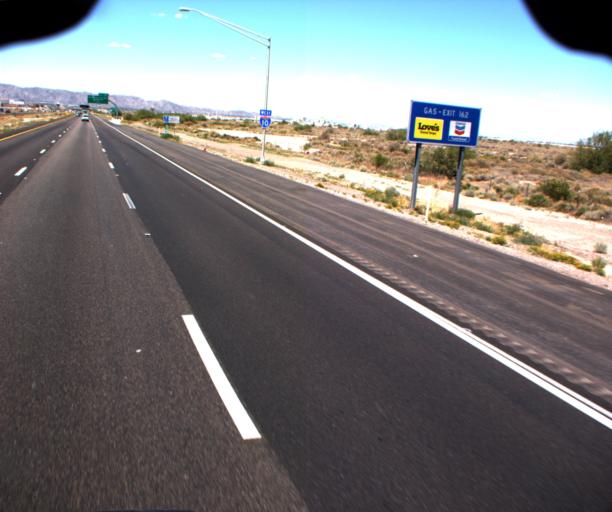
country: US
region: Arizona
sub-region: Maricopa County
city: Sun Lakes
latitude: 33.2613
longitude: -111.9525
